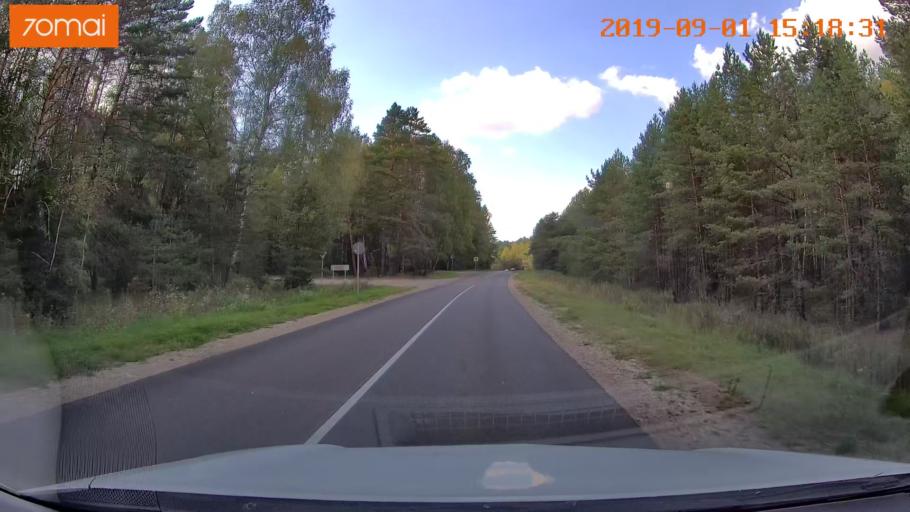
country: RU
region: Kaluga
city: Maloyaroslavets
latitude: 54.9080
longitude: 36.5079
